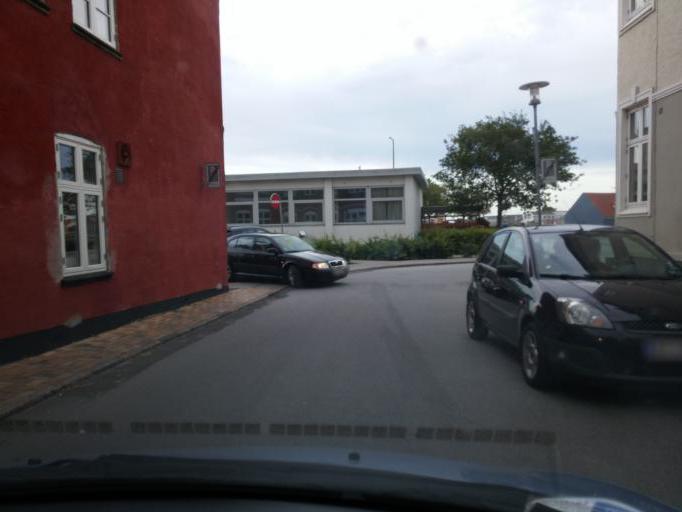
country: DK
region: South Denmark
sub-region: Kerteminde Kommune
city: Kerteminde
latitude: 55.4499
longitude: 10.6592
